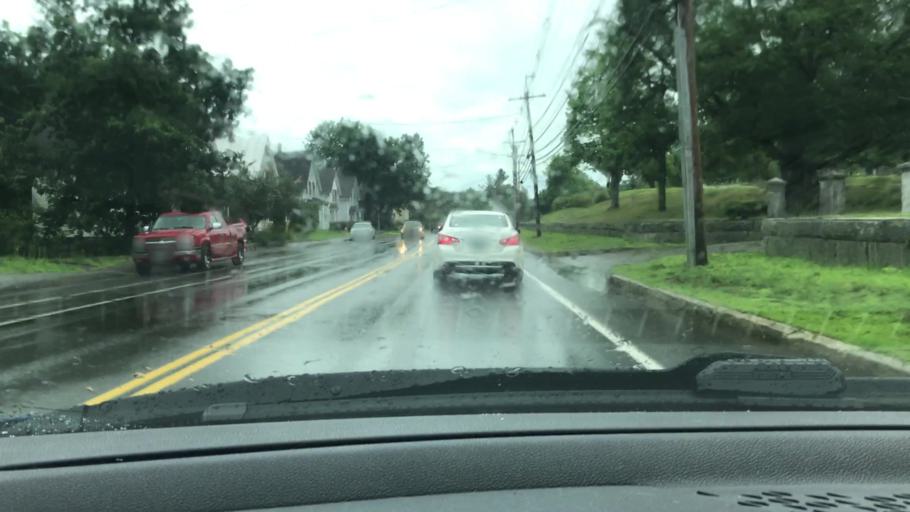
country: US
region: New Hampshire
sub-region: Merrimack County
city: Concord
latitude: 43.2235
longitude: -71.5523
